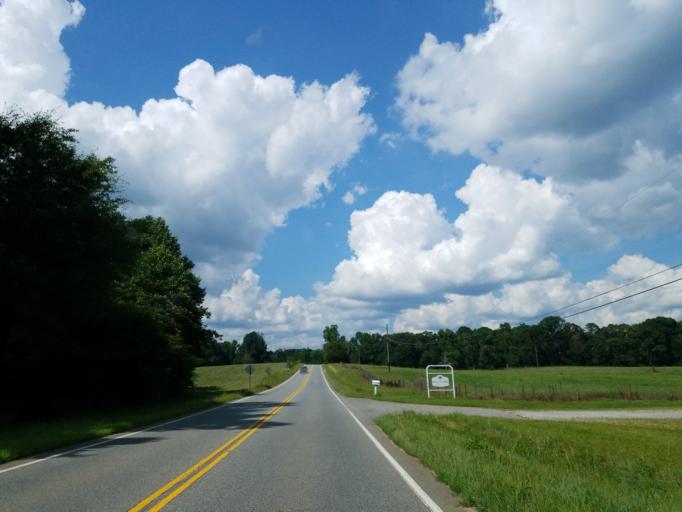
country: US
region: Georgia
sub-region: Dawson County
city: Dawsonville
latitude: 34.4330
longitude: -84.1021
